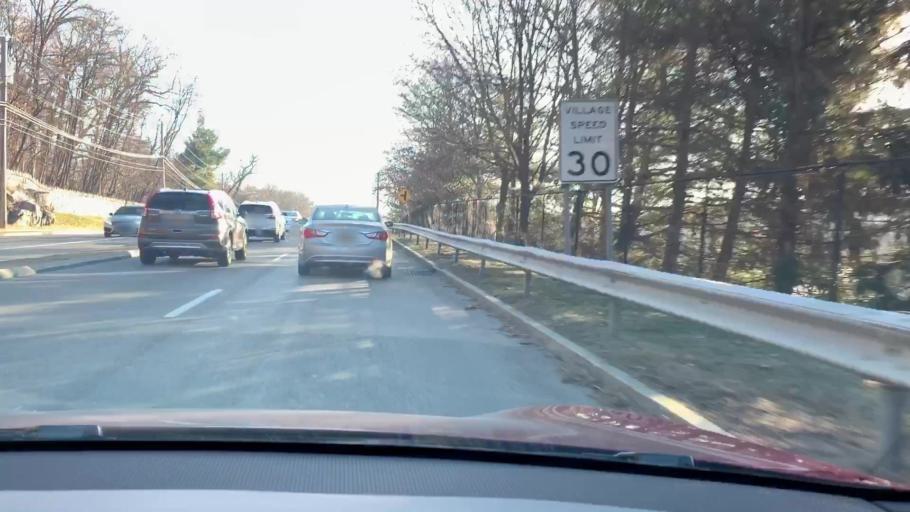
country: US
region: New York
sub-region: Westchester County
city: Tarrytown
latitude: 41.0641
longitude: -73.8497
